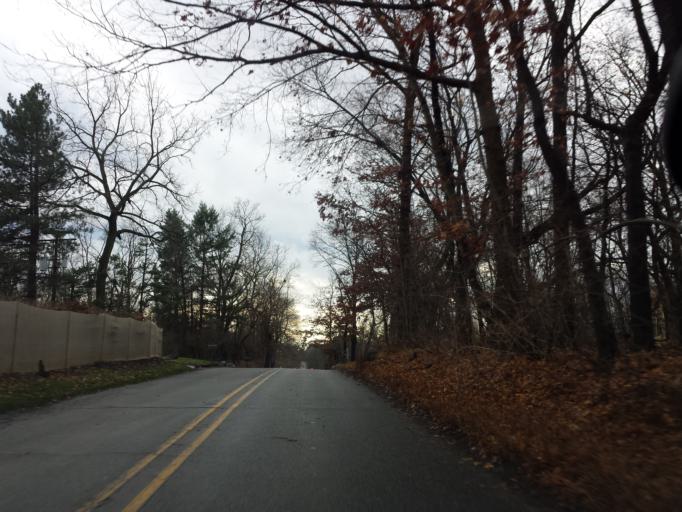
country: US
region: Michigan
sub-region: Oakland County
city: Bloomfield Hills
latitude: 42.5830
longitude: -83.2653
